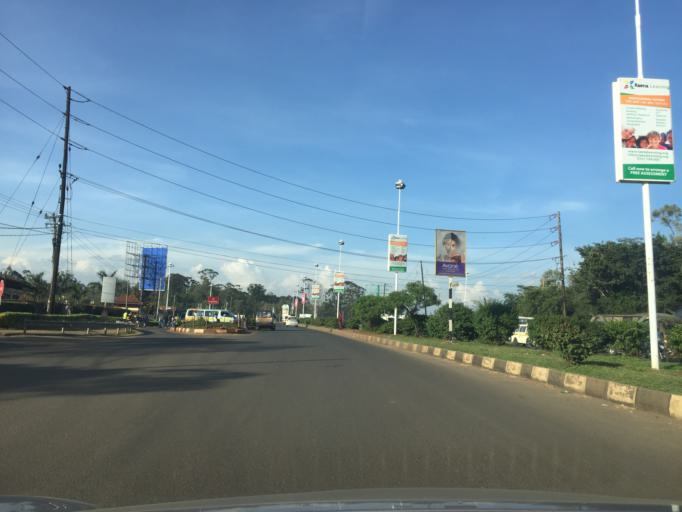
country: KE
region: Nairobi Area
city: Nairobi
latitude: -1.3446
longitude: 36.7661
